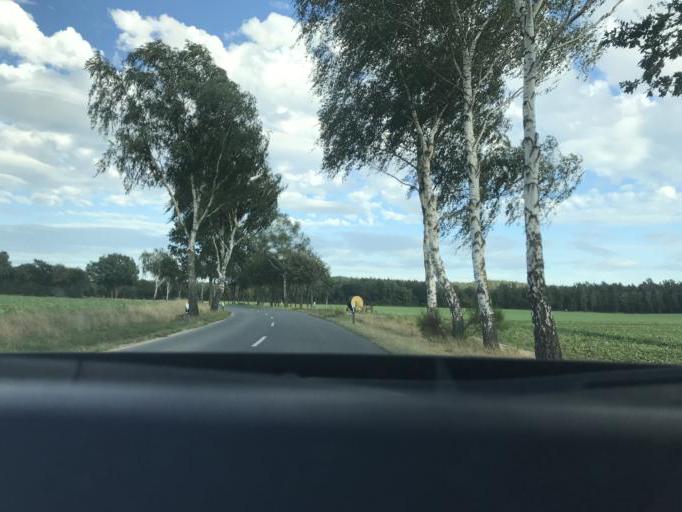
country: DE
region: Lower Saxony
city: Suderburg
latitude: 52.8898
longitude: 10.4737
